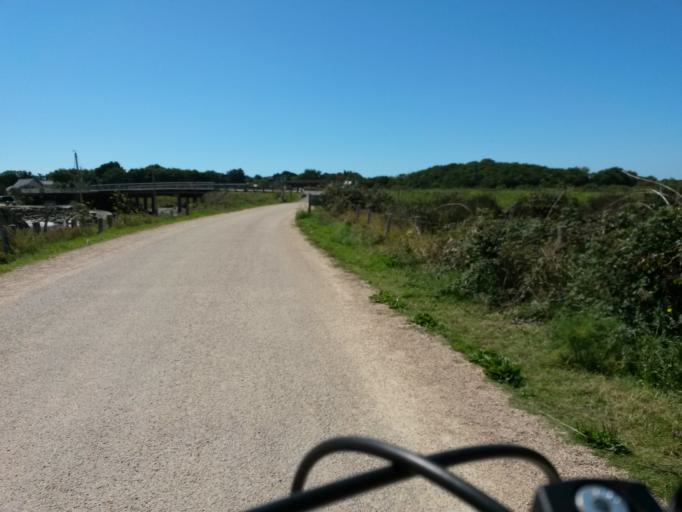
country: FR
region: Pays de la Loire
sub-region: Departement de la Loire-Atlantique
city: Mesquer
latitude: 47.4113
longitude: -2.4645
